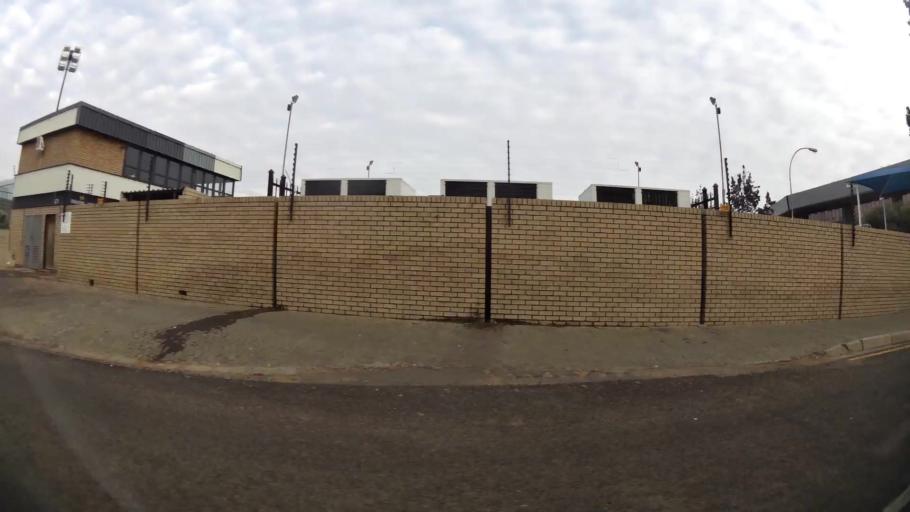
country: ZA
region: Orange Free State
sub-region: Mangaung Metropolitan Municipality
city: Bloemfontein
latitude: -29.1137
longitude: 26.1891
